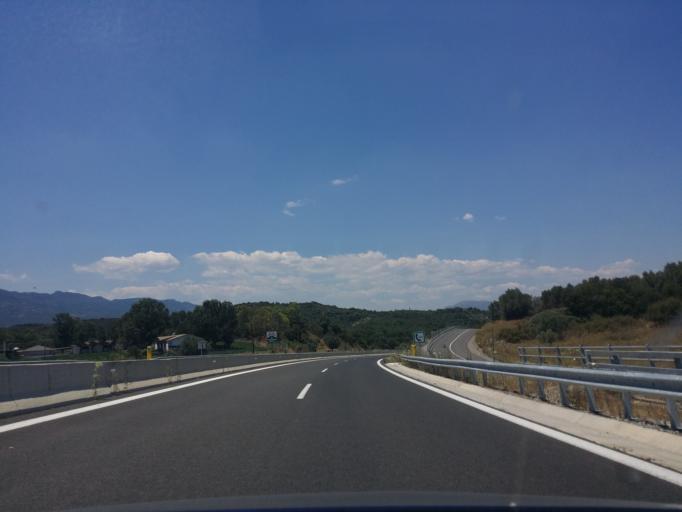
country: GR
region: Peloponnese
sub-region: Nomos Lakonias
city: Magoula
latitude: 37.1637
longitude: 22.3642
